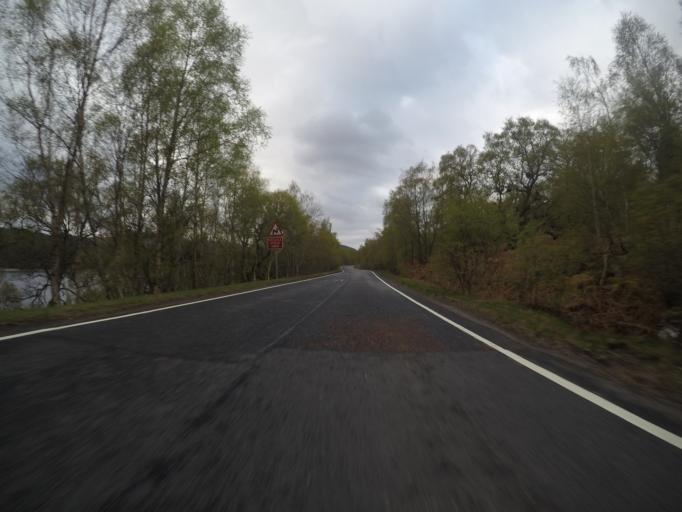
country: GB
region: Scotland
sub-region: Highland
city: Kingussie
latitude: 56.9680
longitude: -4.4397
